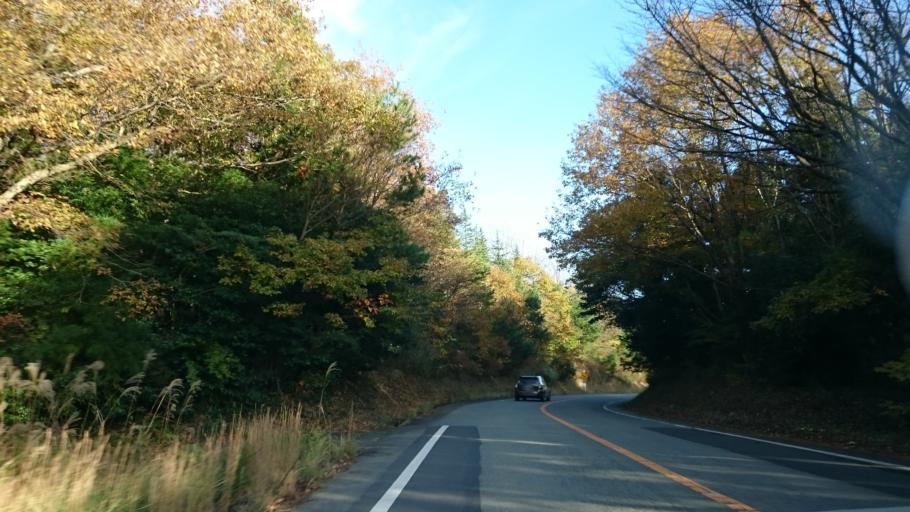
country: JP
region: Shizuoka
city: Heda
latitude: 34.9748
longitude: 138.9034
